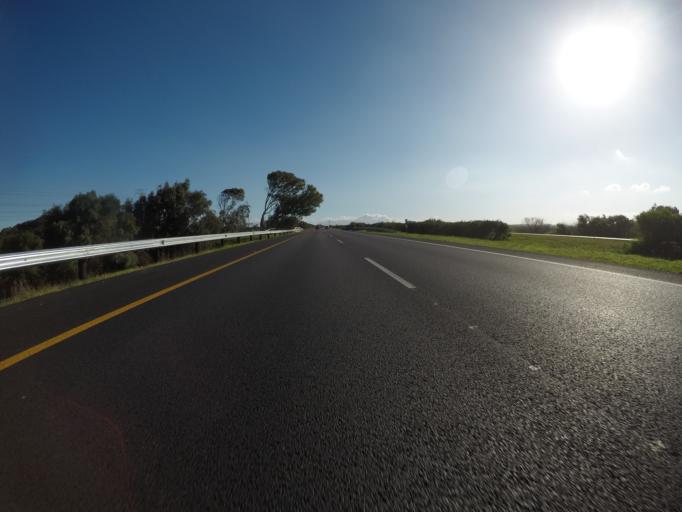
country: ZA
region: Western Cape
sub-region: Cape Winelands District Municipality
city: Stellenbosch
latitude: -34.0436
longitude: 18.7390
